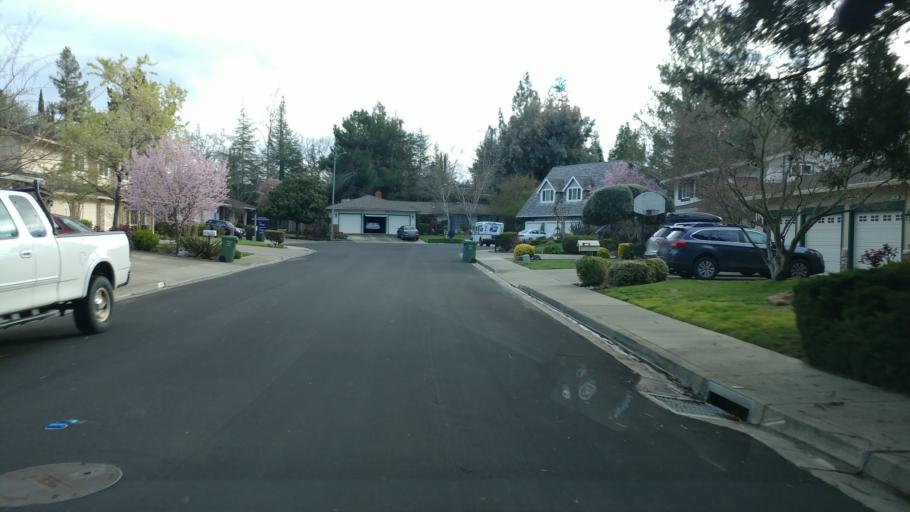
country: US
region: California
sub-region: Contra Costa County
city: Diablo
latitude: 37.8208
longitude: -121.9762
